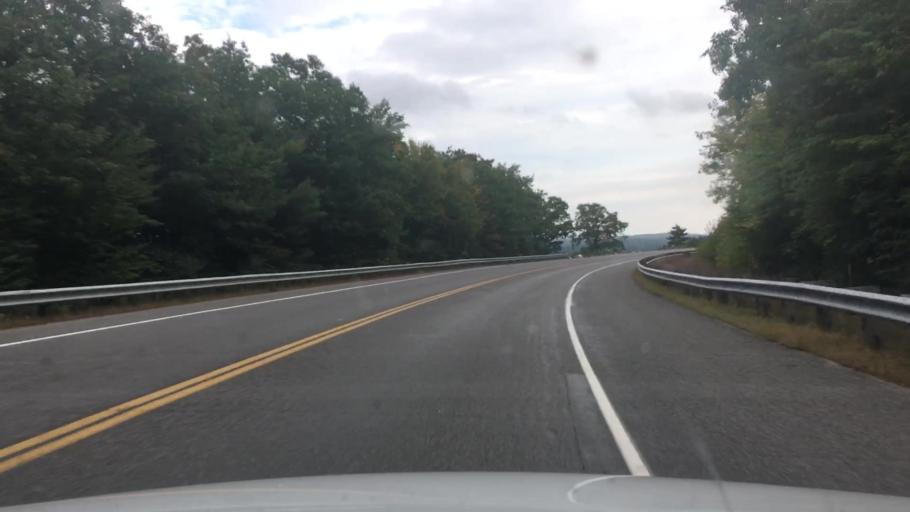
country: US
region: New Hampshire
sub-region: Carroll County
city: Wolfeboro
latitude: 43.5169
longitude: -71.2682
